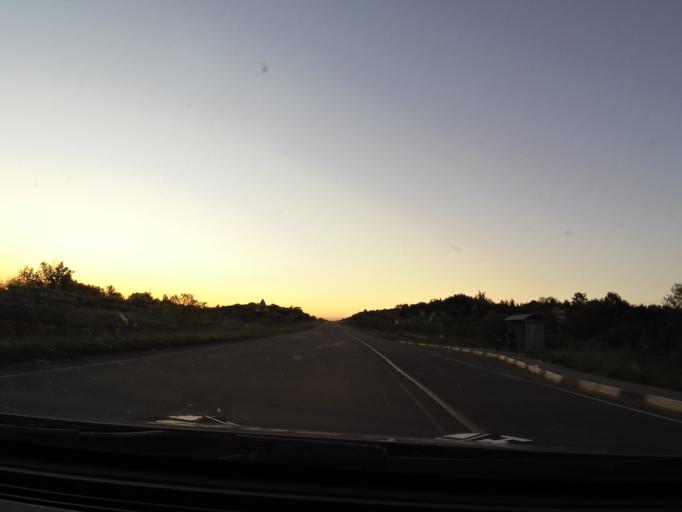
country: RU
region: Vologda
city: Vytegra
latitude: 60.9289
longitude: 36.0912
